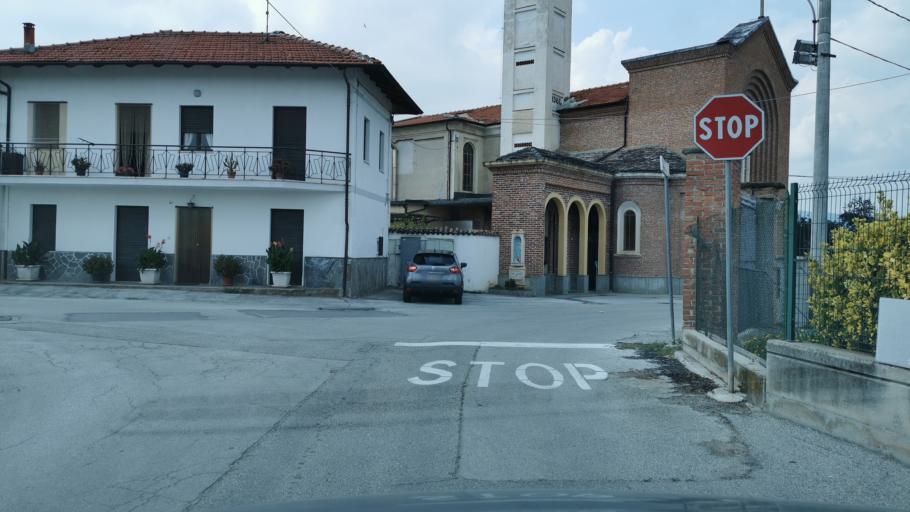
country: IT
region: Piedmont
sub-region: Provincia di Cuneo
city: Caraglio
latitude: 44.4306
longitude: 7.4500
